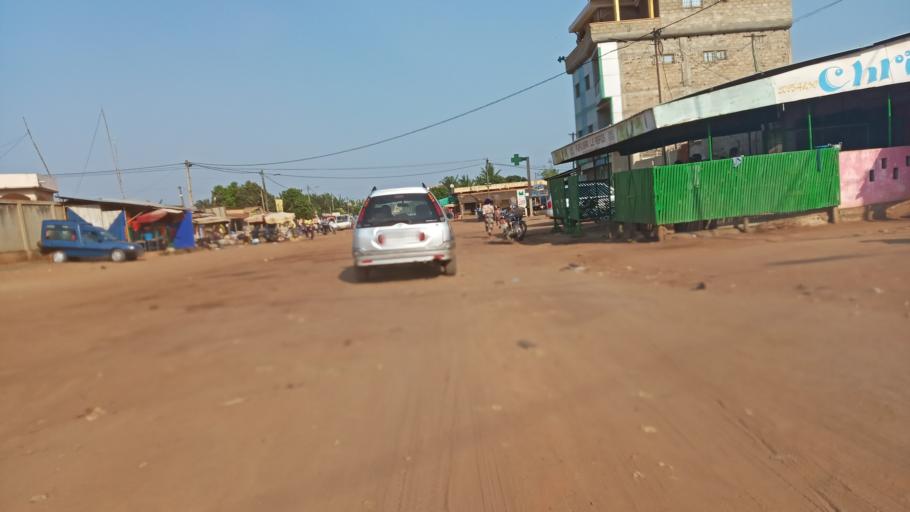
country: TG
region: Maritime
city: Lome
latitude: 6.1806
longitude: 1.1630
